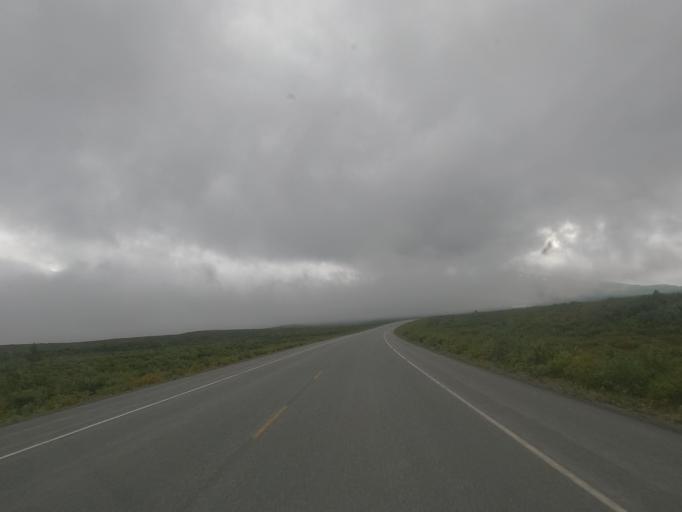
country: US
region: Alaska
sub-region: Haines Borough
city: Haines
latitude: 59.7965
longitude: -136.6050
